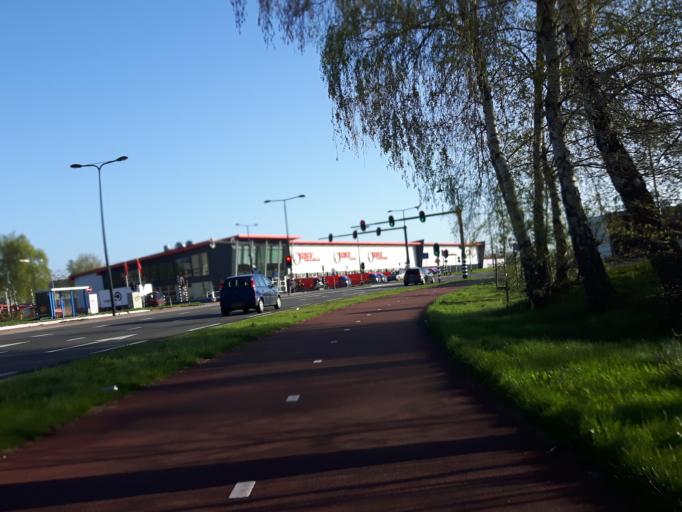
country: NL
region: Overijssel
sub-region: Gemeente Hengelo
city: Hengelo
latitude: 52.2293
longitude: 6.8379
